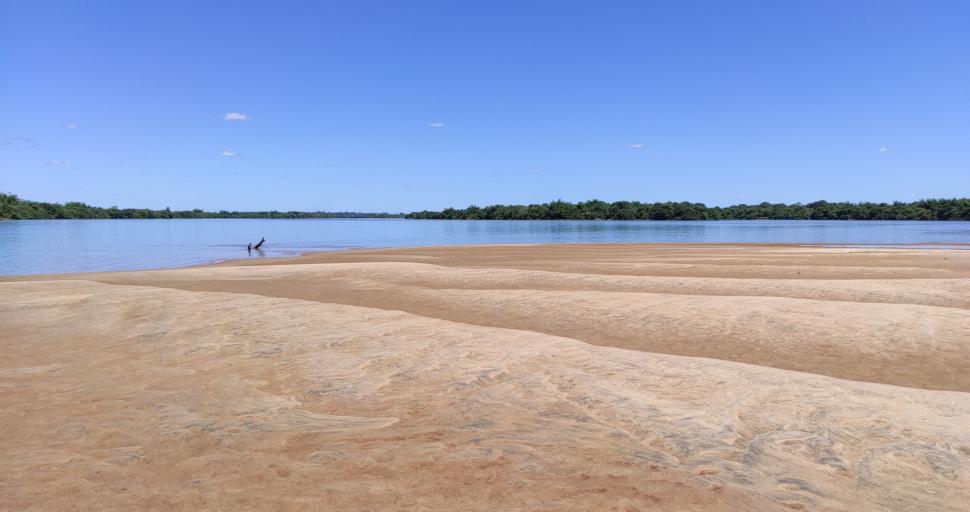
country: AR
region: Corrientes
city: Ituzaingo
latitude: -27.5480
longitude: -56.6976
